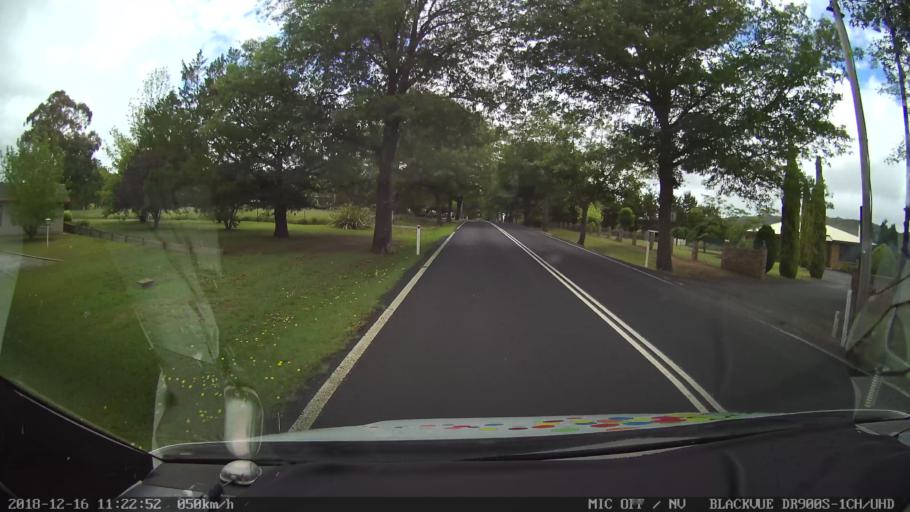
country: AU
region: New South Wales
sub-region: Tenterfield Municipality
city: Carrolls Creek
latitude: -29.0533
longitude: 152.0304
